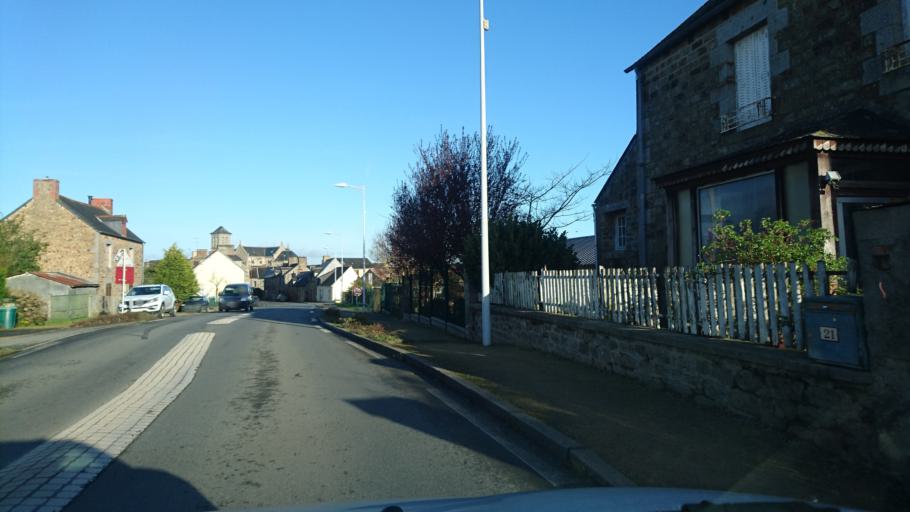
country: FR
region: Brittany
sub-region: Departement d'Ille-et-Vilaine
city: La Boussac
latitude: 48.5121
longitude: -1.6575
